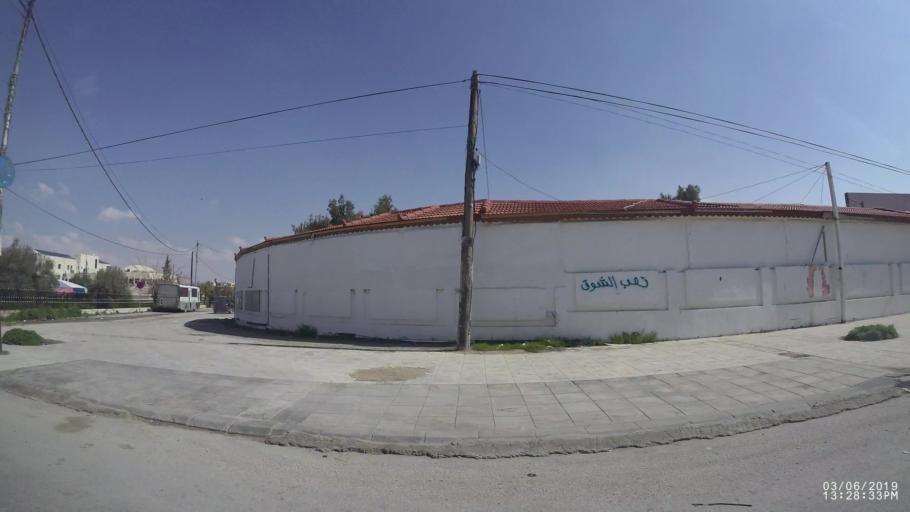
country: JO
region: Zarqa
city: Zarqa
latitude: 32.0754
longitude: 36.1009
